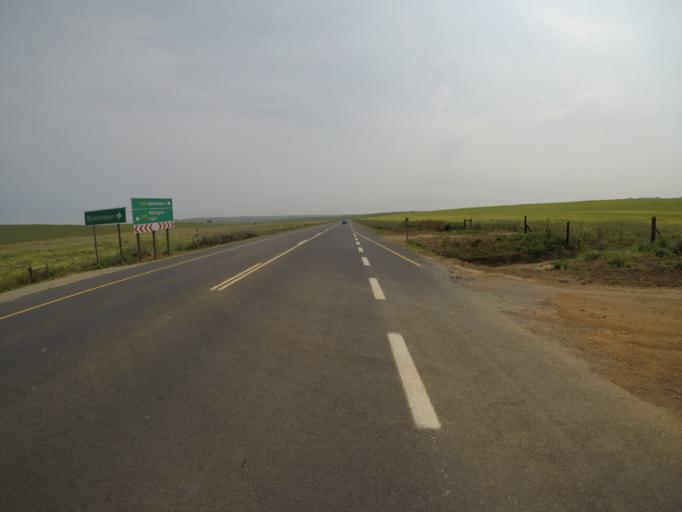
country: ZA
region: Western Cape
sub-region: West Coast District Municipality
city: Malmesbury
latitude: -33.4633
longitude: 18.7879
